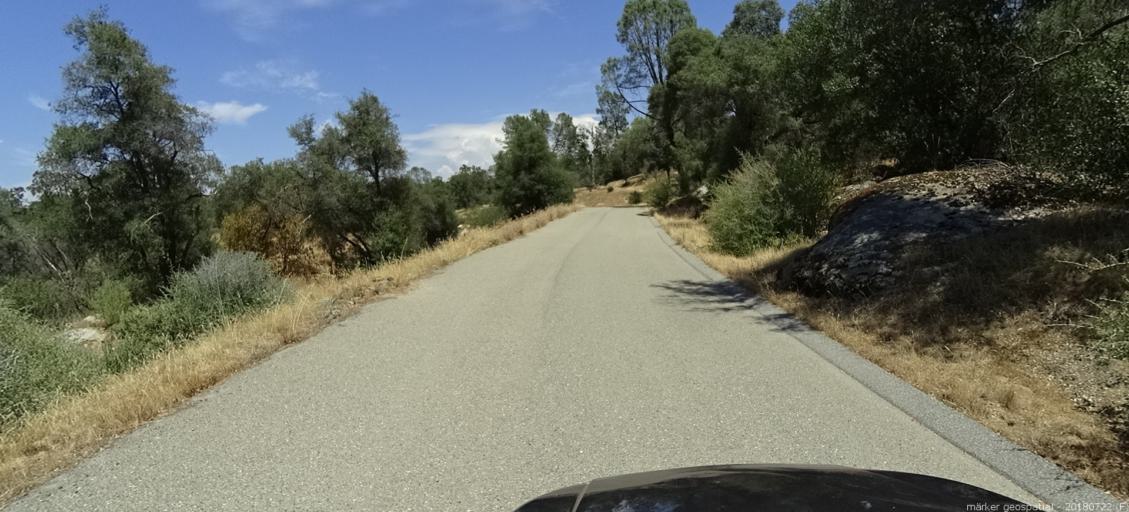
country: US
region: California
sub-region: Madera County
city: Yosemite Lakes
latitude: 37.2073
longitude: -119.7246
